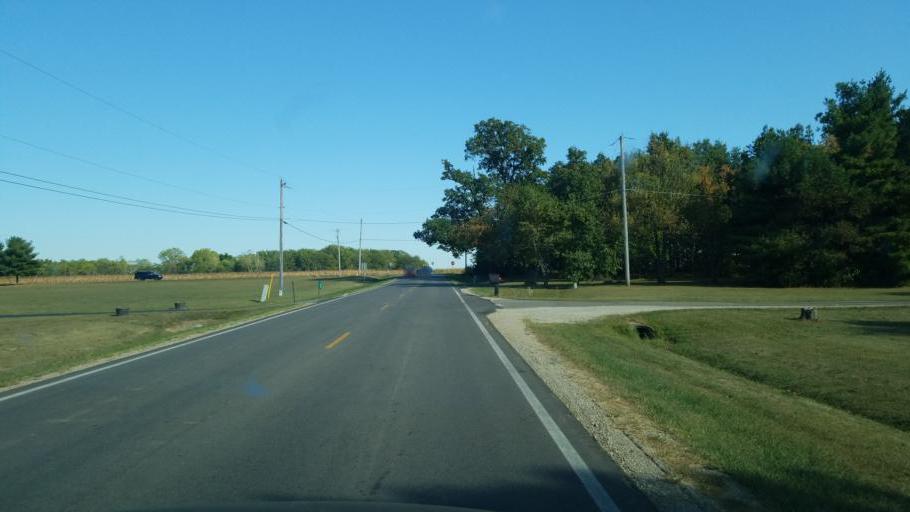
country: US
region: Ohio
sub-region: Madison County
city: Choctaw Lake
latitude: 39.9470
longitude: -83.4748
